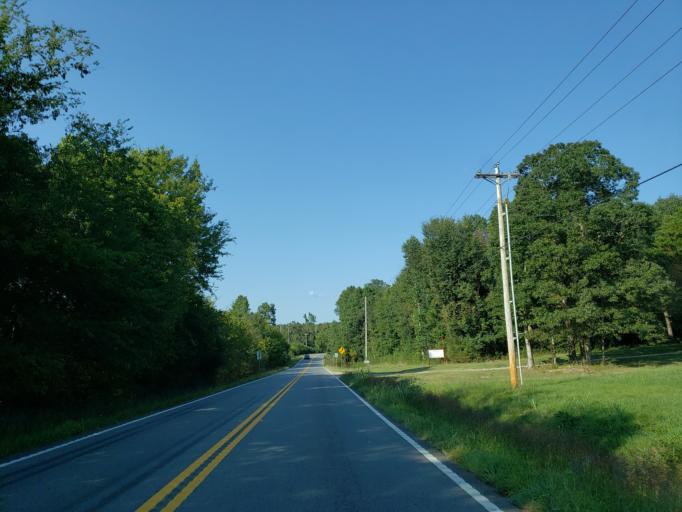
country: US
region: Tennessee
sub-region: Bradley County
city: Wildwood Lake
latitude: 34.9437
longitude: -84.7809
